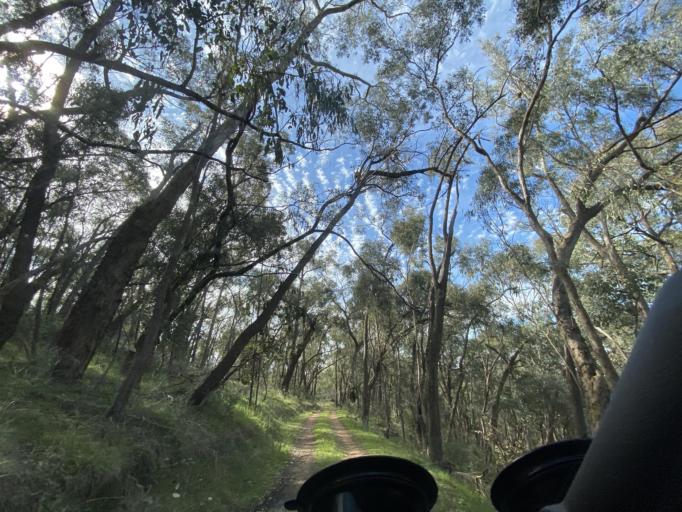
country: AU
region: Victoria
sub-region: Mansfield
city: Mansfield
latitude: -36.8057
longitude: 146.1191
